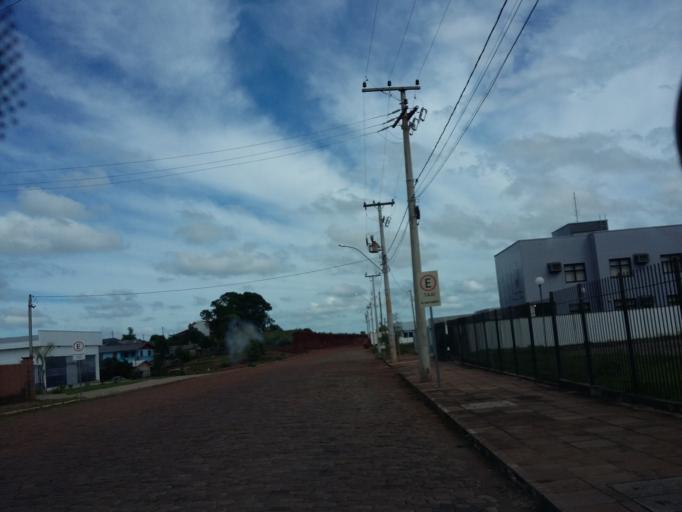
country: BR
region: Rio Grande do Sul
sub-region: Lagoa Vermelha
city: Lagoa Vermelha
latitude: -28.2022
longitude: -51.5206
